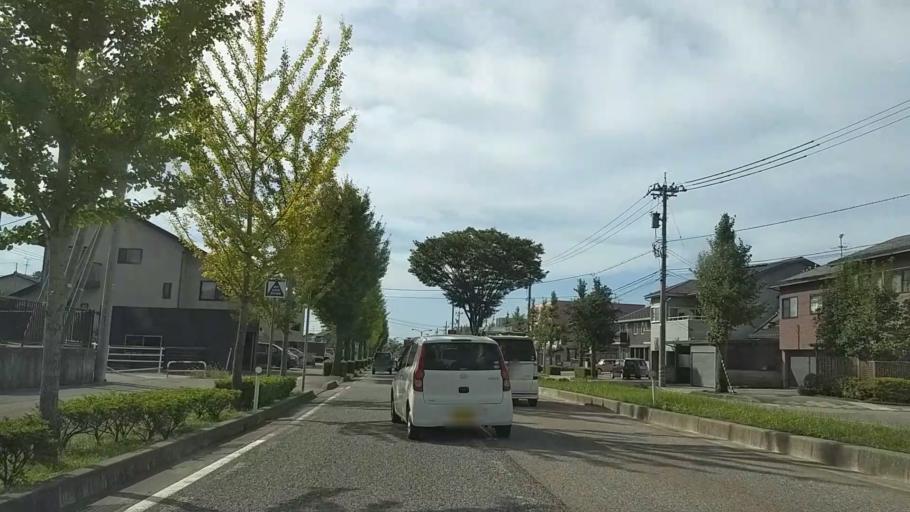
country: JP
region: Ishikawa
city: Nonoichi
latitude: 36.5350
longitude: 136.6617
